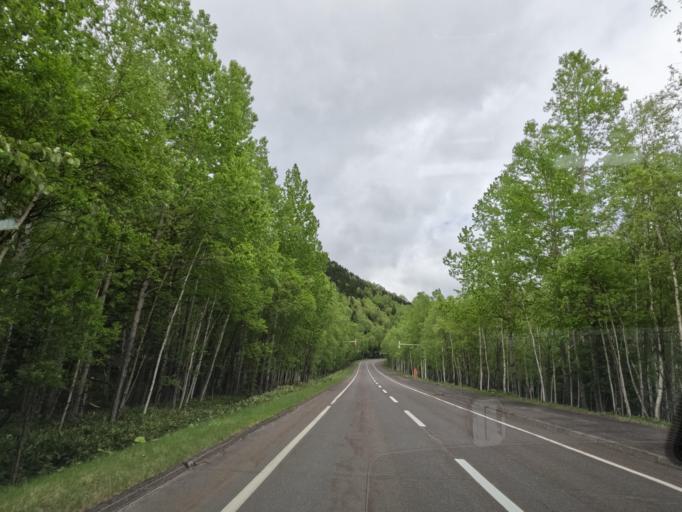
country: JP
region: Hokkaido
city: Kamikawa
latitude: 43.6443
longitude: 143.0197
